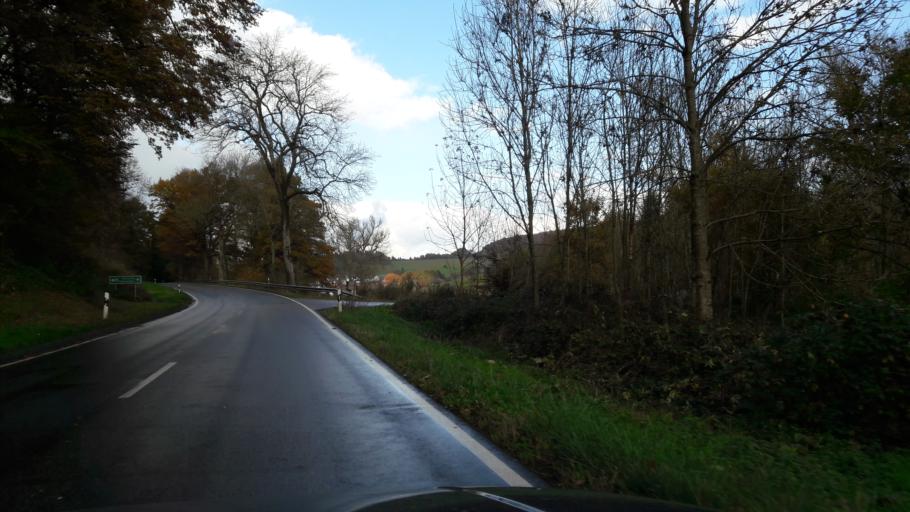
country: DE
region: Rheinland-Pfalz
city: Ohmbach
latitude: 49.4596
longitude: 7.3483
